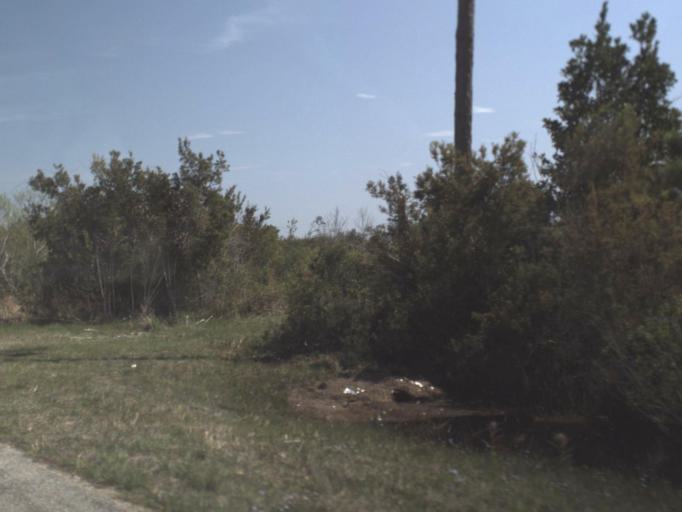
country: US
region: Florida
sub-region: Franklin County
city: Apalachicola
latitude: 29.7254
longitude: -85.0820
